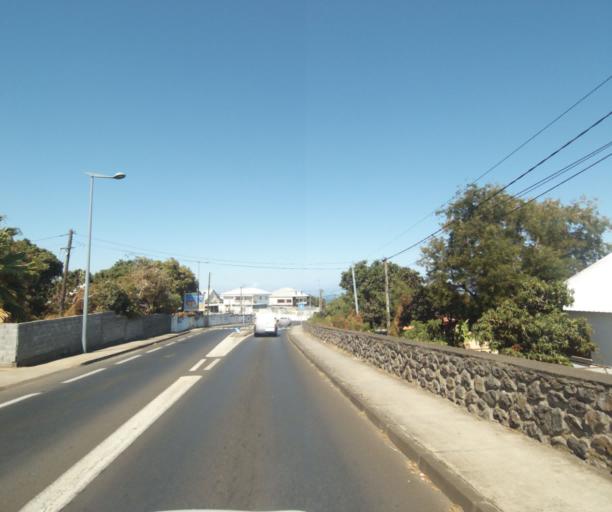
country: RE
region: Reunion
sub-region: Reunion
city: La Possession
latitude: -20.9777
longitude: 55.3249
